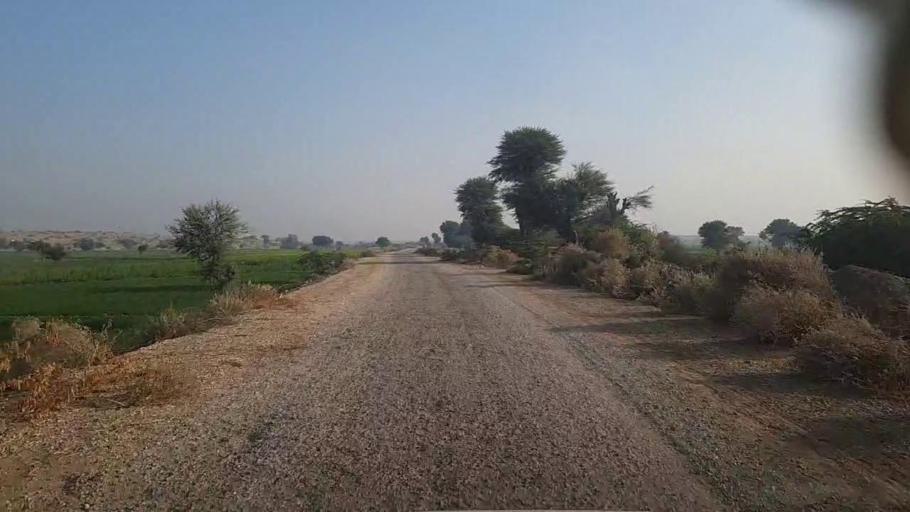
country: PK
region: Sindh
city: Karaundi
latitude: 26.7263
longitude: 68.4881
